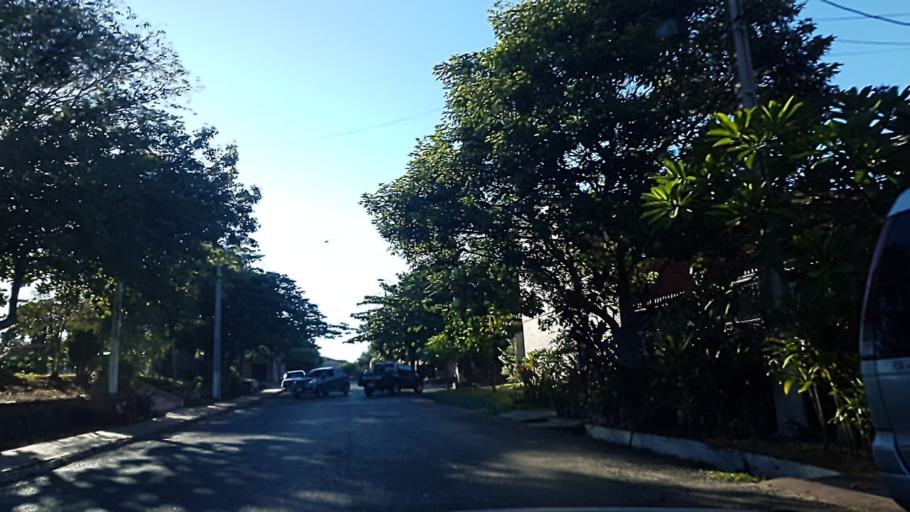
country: PY
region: Asuncion
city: Asuncion
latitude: -25.2715
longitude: -57.5756
